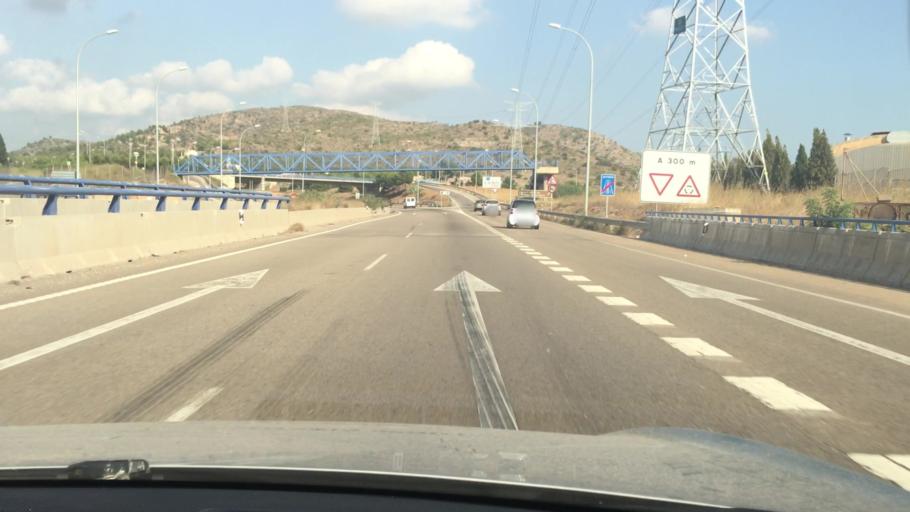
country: ES
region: Valencia
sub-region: Provincia de Castello
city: Borriol
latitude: 40.0129
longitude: -0.0956
